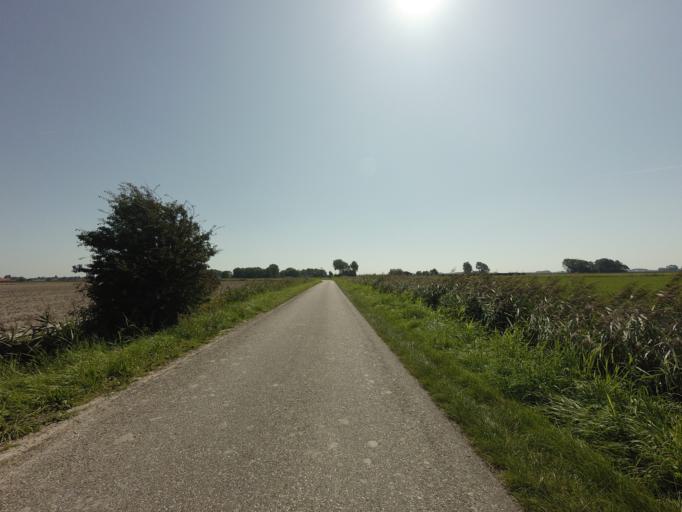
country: NL
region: Friesland
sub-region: Gemeente Dongeradeel
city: Ternaard
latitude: 53.3832
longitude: 6.0288
